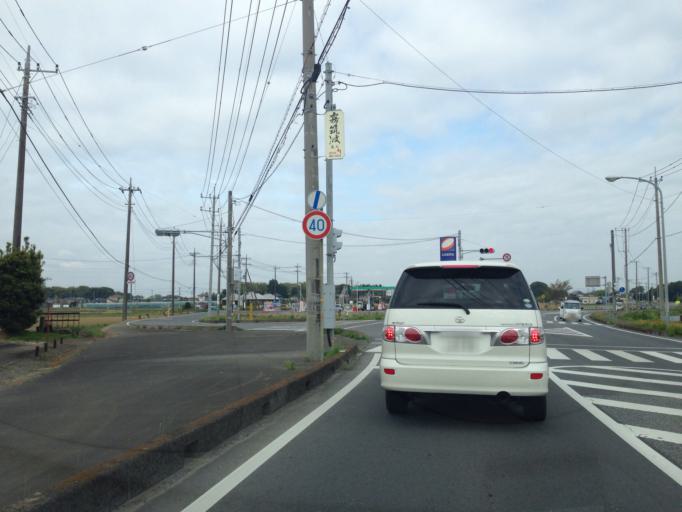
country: JP
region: Ibaraki
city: Ishige
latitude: 36.1439
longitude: 140.0307
